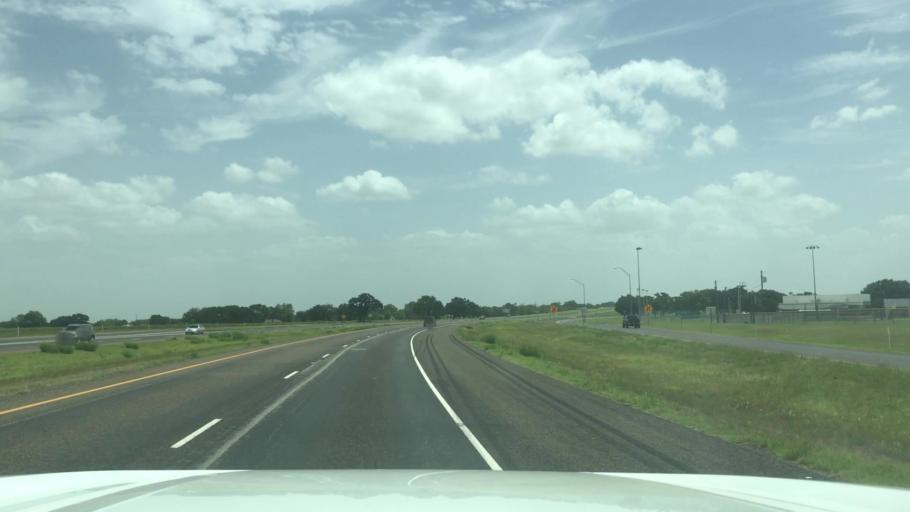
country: US
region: Texas
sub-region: Falls County
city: Marlin
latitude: 31.3137
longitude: -96.8759
